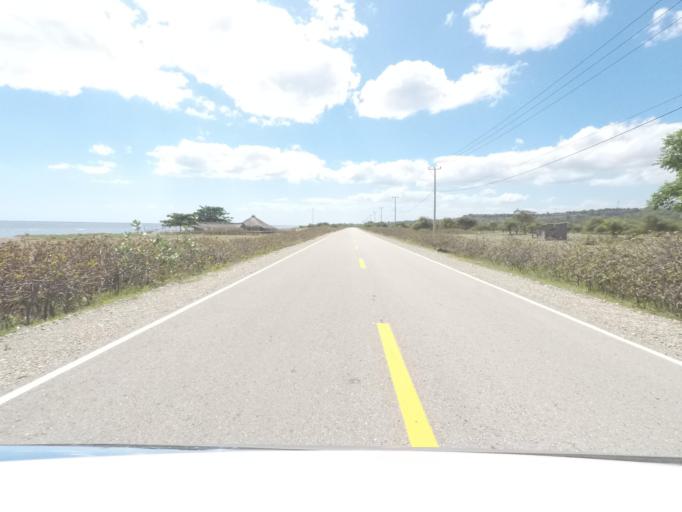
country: TL
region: Baucau
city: Baucau
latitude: -8.4451
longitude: 126.6479
